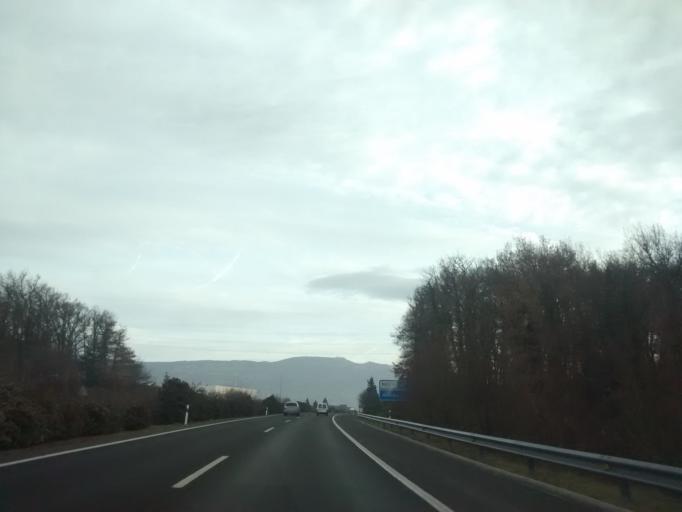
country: ES
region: Navarre
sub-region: Provincia de Navarra
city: Arbizu
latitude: 42.9047
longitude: -2.0491
